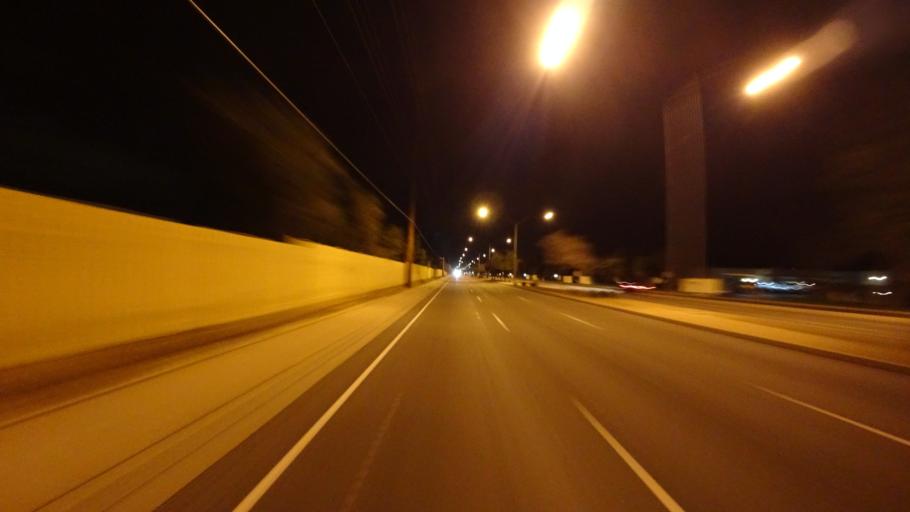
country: US
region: Arizona
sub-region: Maricopa County
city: Gilbert
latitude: 33.4022
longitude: -111.6847
